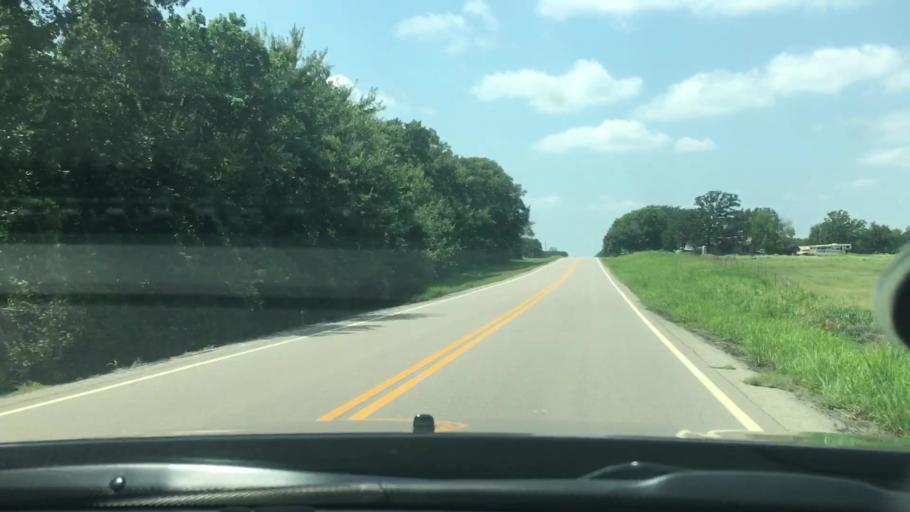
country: US
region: Oklahoma
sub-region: Coal County
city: Coalgate
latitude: 34.3683
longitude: -96.3401
